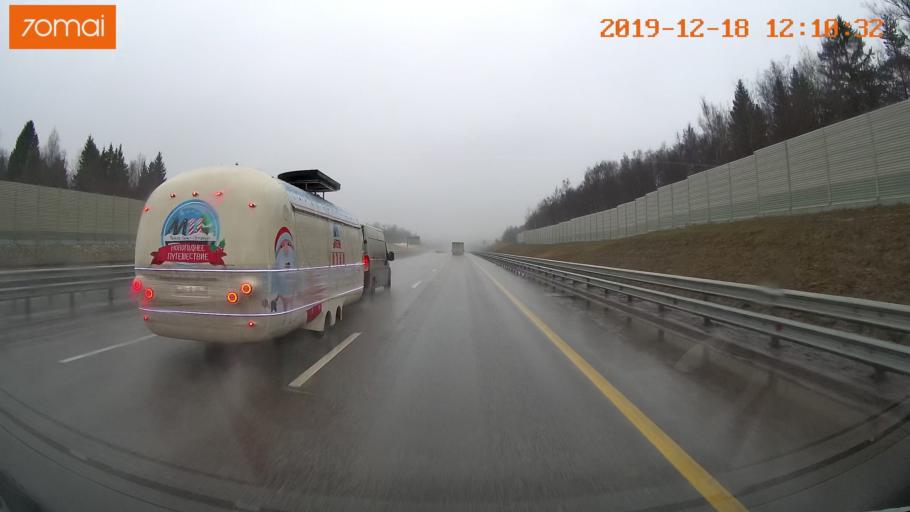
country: RU
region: Moskovskaya
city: Rumyantsevo
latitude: 55.9197
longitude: 36.5890
